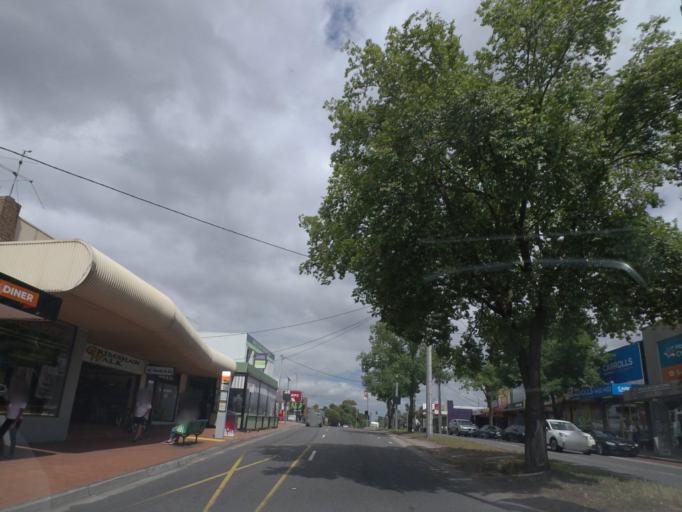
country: AU
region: Victoria
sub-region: Banyule
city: Greensborough
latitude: -37.7045
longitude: 145.1019
